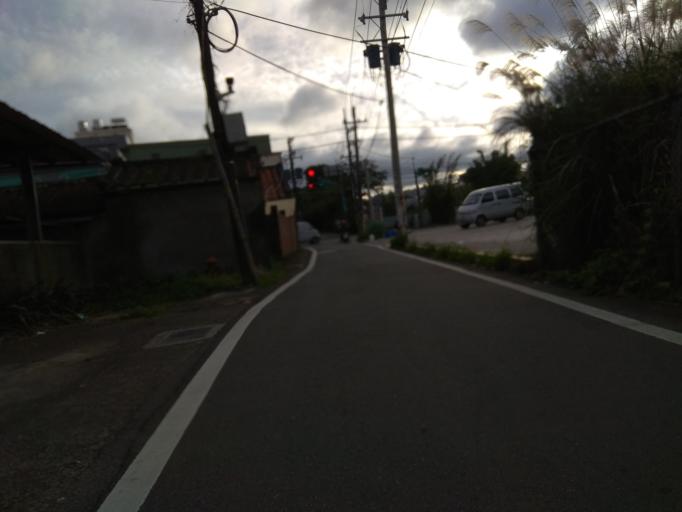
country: TW
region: Taiwan
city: Daxi
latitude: 24.9226
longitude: 121.1920
